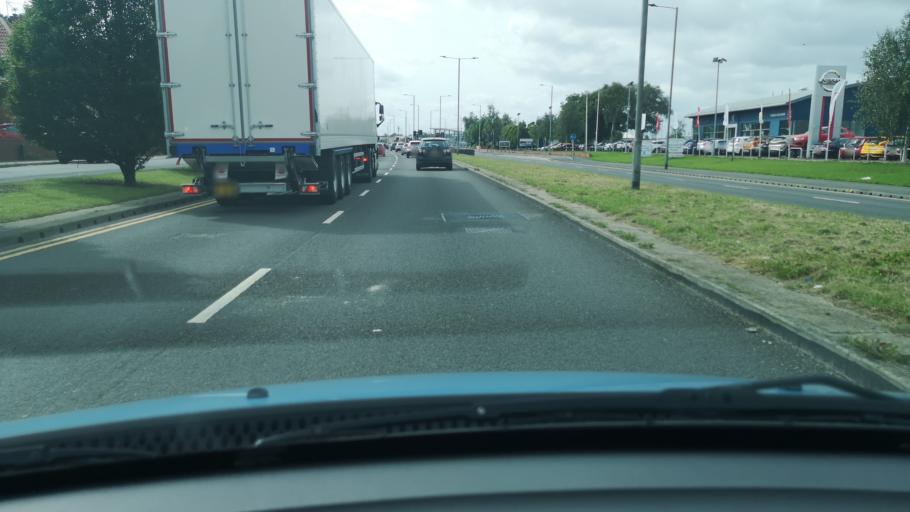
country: GB
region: England
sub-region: Doncaster
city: Doncaster
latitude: 53.5384
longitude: -1.1170
